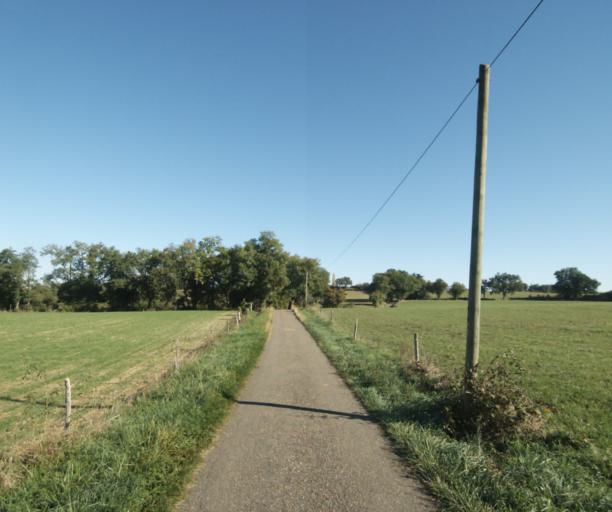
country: FR
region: Midi-Pyrenees
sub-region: Departement du Gers
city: Gondrin
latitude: 43.8228
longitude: 0.2576
